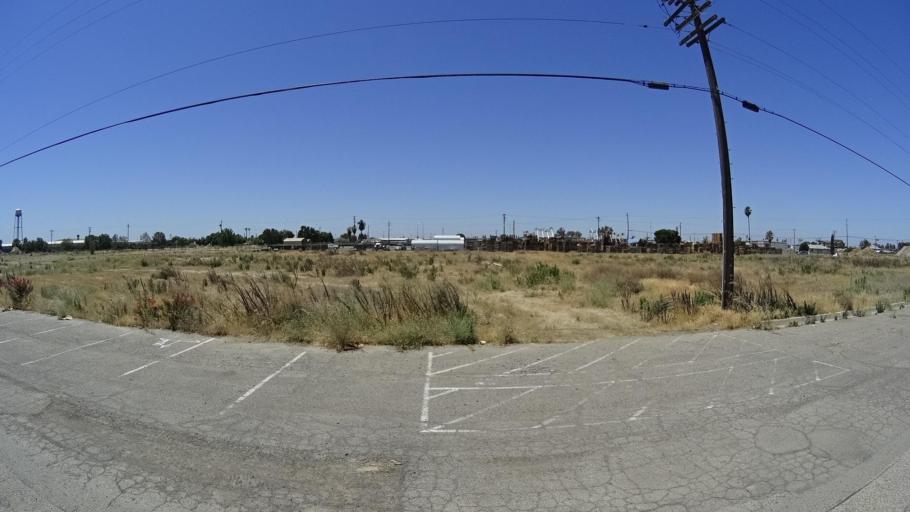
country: US
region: California
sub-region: Fresno County
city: Fresno
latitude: 36.7030
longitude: -119.7617
